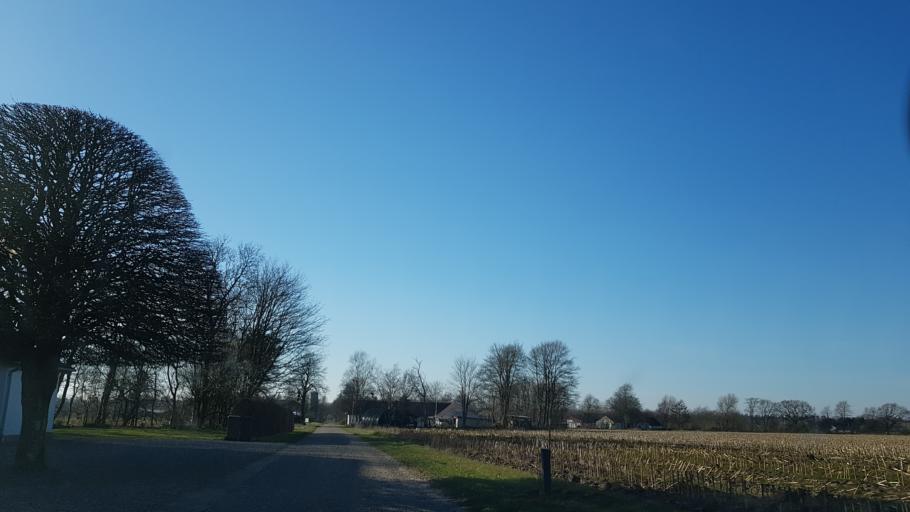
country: DK
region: South Denmark
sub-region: Vejen Kommune
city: Holsted
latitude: 55.4340
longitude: 8.9396
